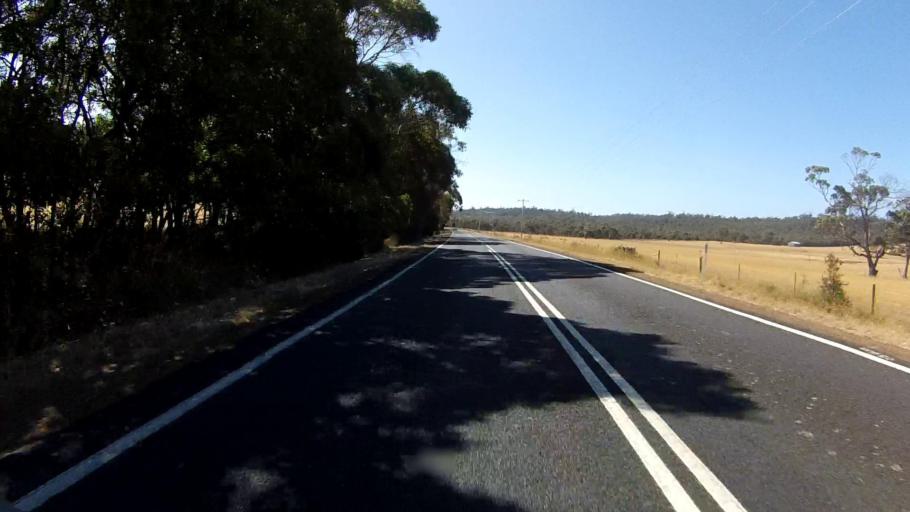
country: AU
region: Tasmania
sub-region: Sorell
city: Sorell
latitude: -42.4217
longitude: 147.9346
